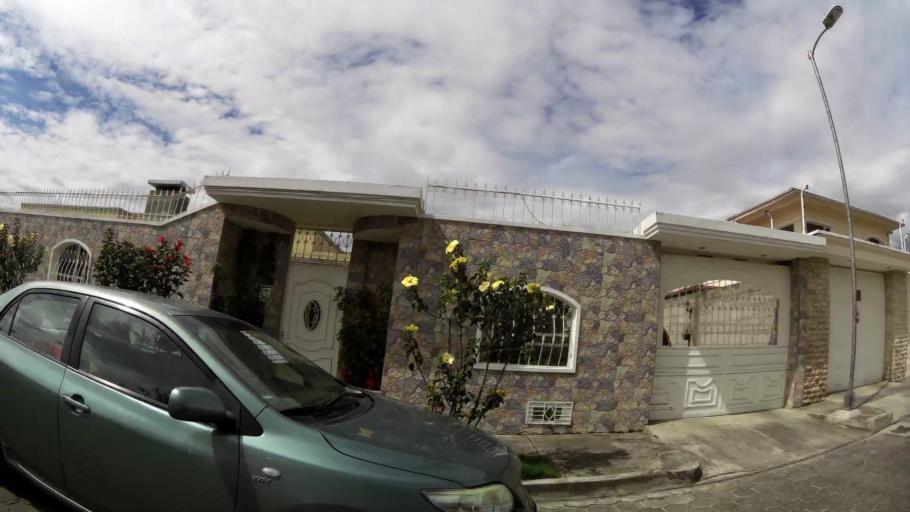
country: EC
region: Cotopaxi
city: Latacunga
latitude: -0.9311
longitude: -78.6012
